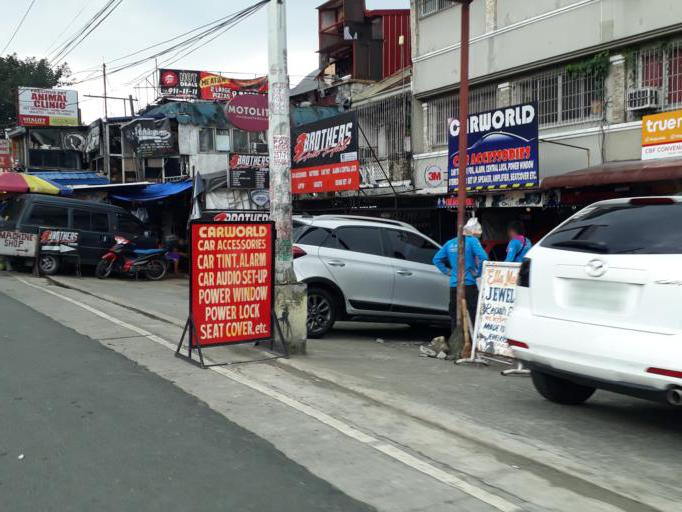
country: PH
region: Metro Manila
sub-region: Quezon City
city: Quezon City
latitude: 14.6697
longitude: 121.0532
